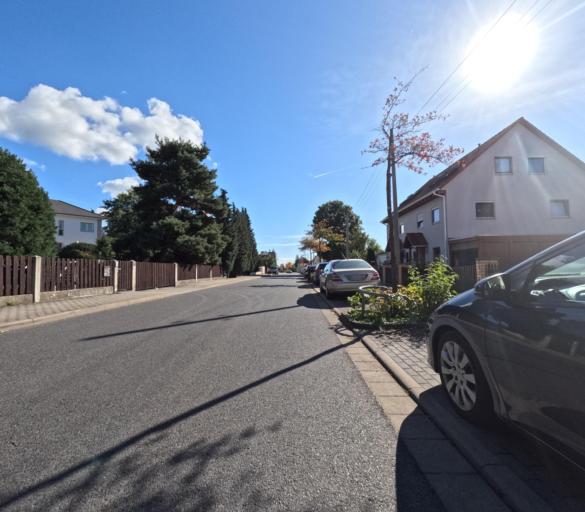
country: DE
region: Saxony
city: Albertstadt
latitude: 51.1157
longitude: 13.7256
